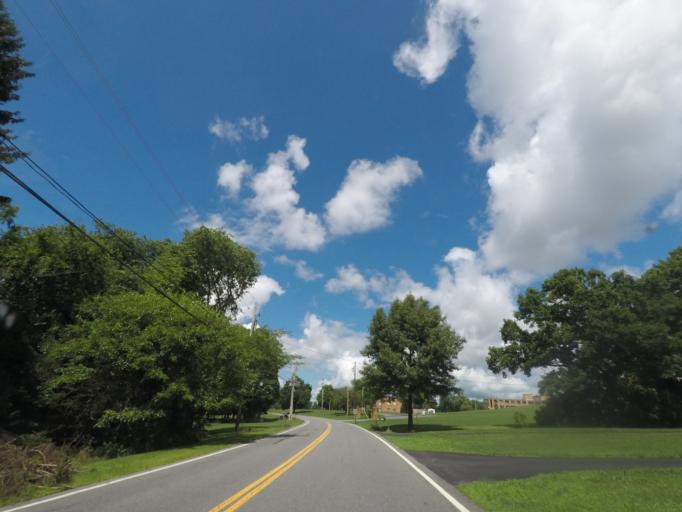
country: US
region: New York
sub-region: Rensselaer County
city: Wynantskill
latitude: 42.6848
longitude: -73.6807
